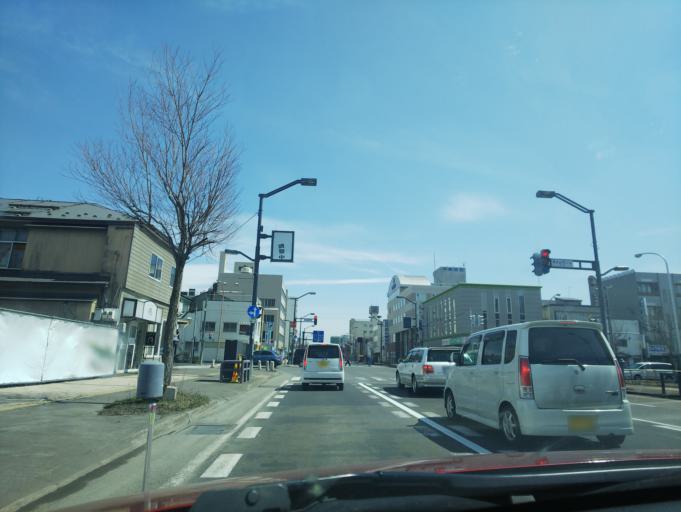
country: JP
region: Hokkaido
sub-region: Asahikawa-shi
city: Asahikawa
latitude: 43.7656
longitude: 142.3727
